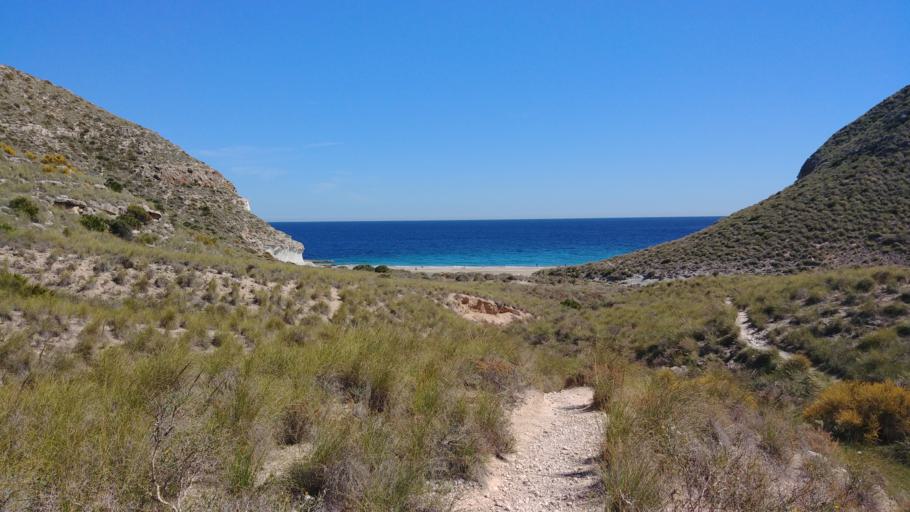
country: ES
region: Andalusia
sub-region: Provincia de Almeria
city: Carboneras
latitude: 36.9343
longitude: -1.9488
